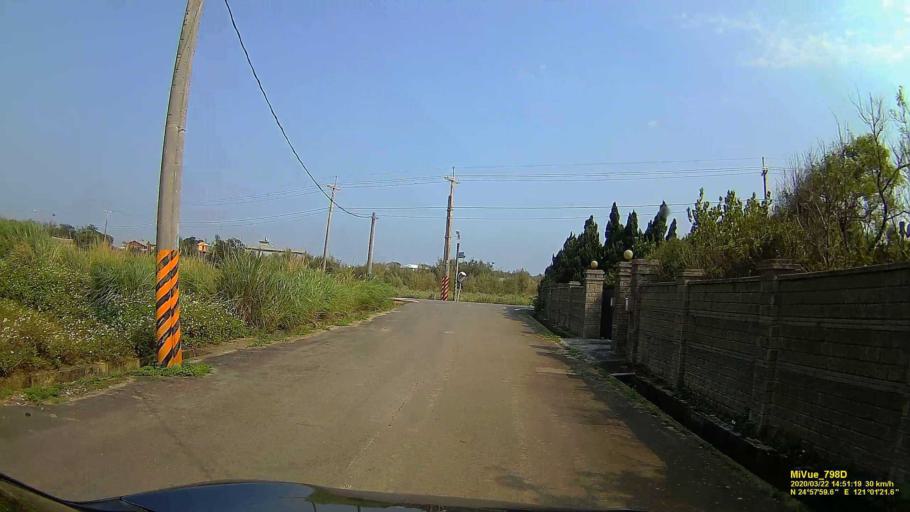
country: TW
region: Taiwan
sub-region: Hsinchu
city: Zhubei
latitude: 24.9665
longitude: 121.0228
